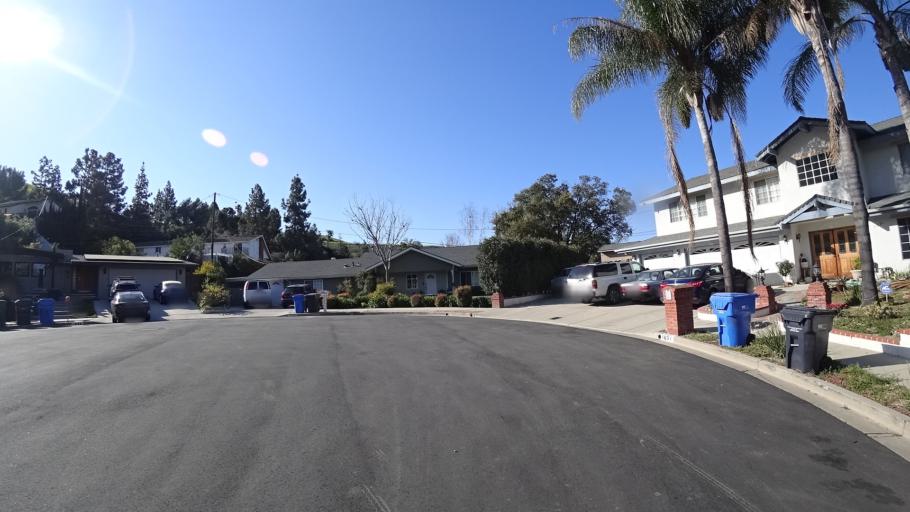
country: US
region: California
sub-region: Ventura County
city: Thousand Oaks
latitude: 34.1898
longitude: -118.8355
